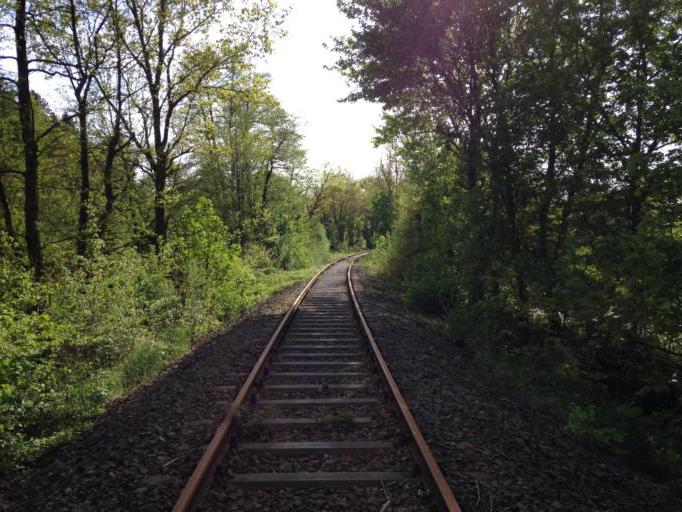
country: DE
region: North Rhine-Westphalia
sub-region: Regierungsbezirk Detmold
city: Lemgo
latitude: 52.0210
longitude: 8.9253
